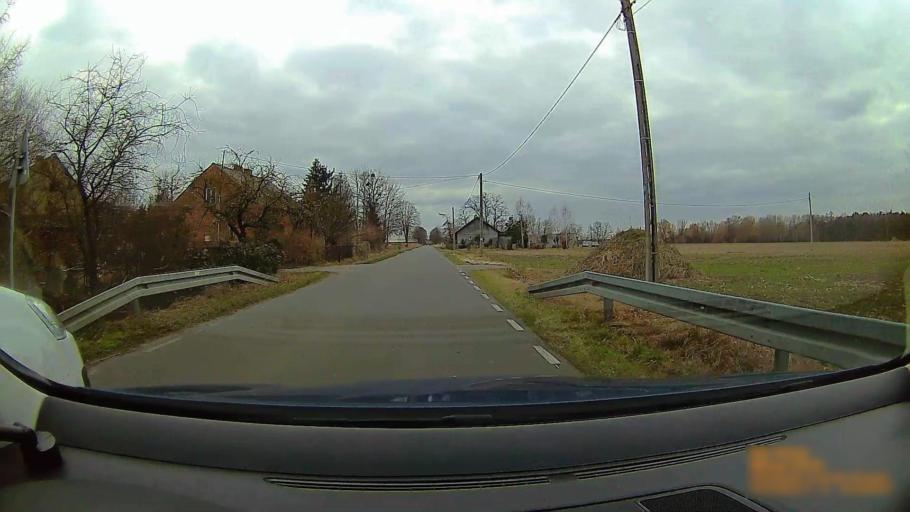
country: PL
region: Greater Poland Voivodeship
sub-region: Powiat koninski
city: Rzgow Pierwszy
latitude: 52.1450
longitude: 18.0554
